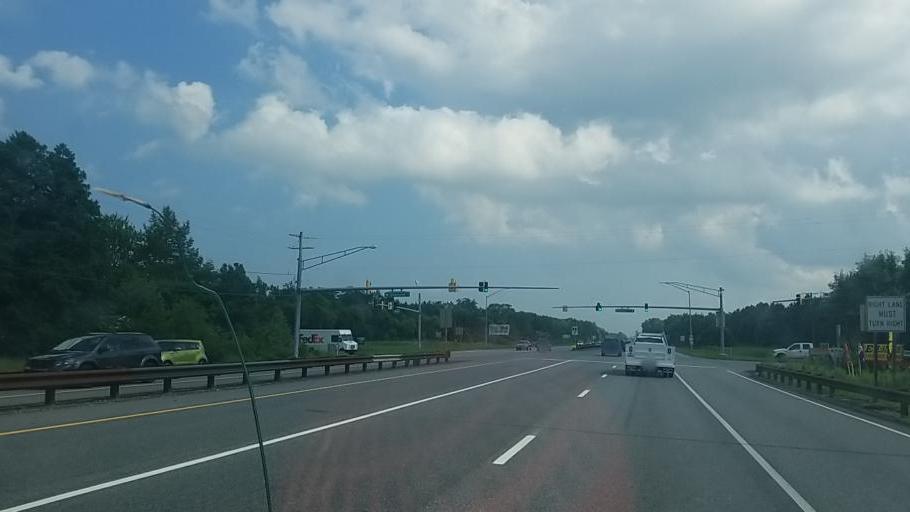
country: US
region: Delaware
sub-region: Sussex County
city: Selbyville
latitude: 38.4415
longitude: -75.2270
